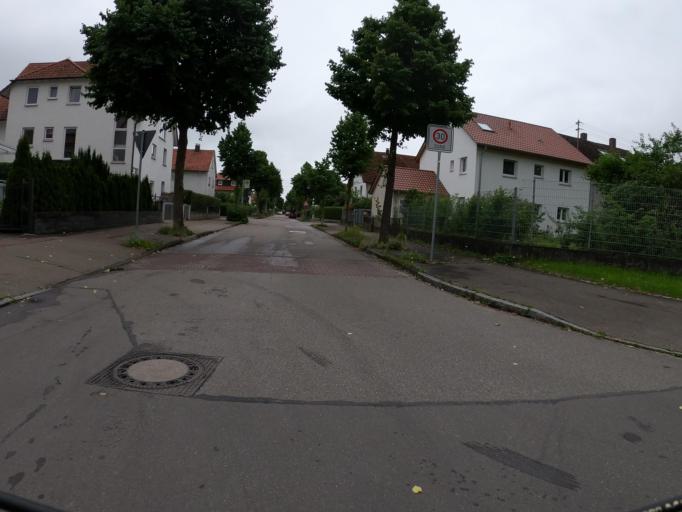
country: DE
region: Baden-Wuerttemberg
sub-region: Tuebingen Region
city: Langenau
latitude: 48.4916
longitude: 10.1147
